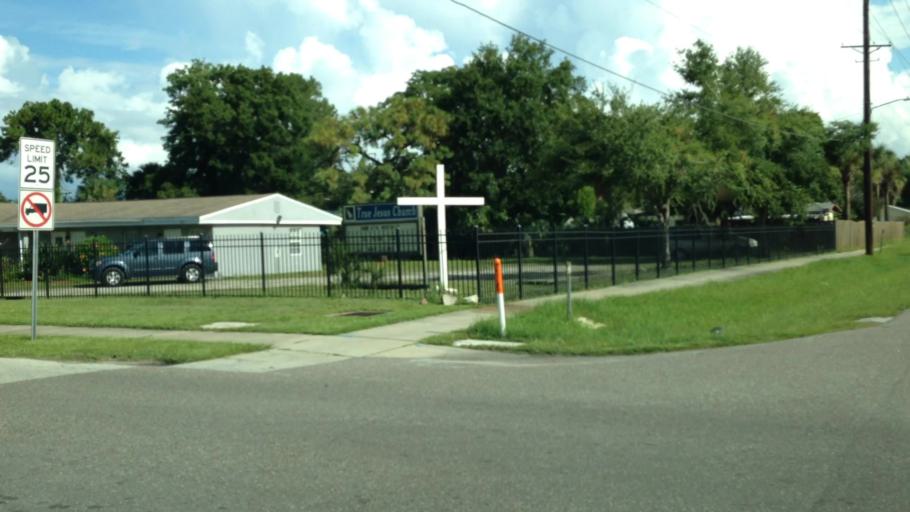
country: US
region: Florida
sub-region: Hillsborough County
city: Tampa
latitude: 27.8876
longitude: -82.5185
